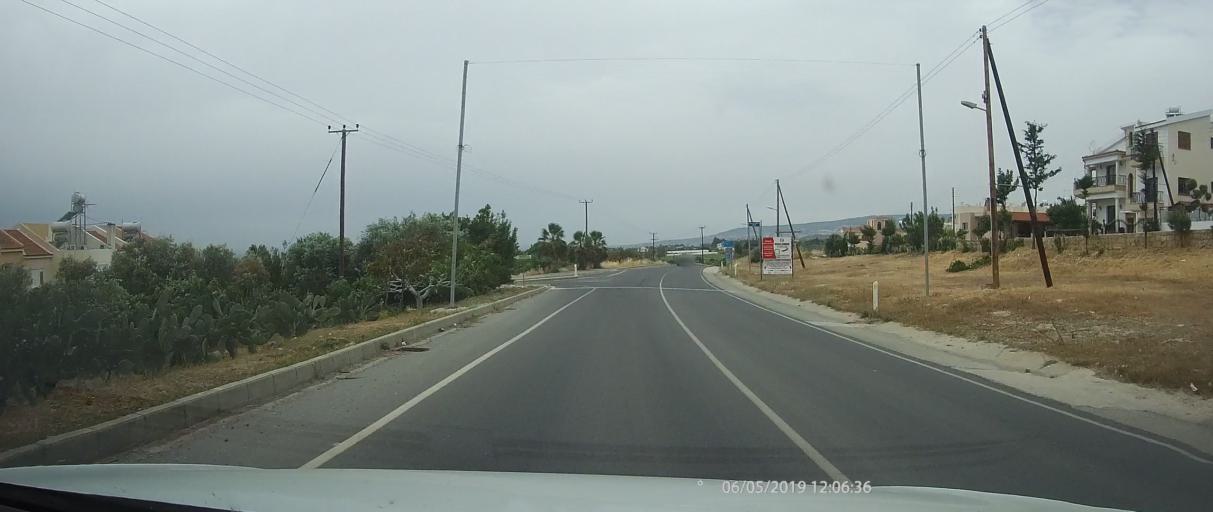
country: CY
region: Pafos
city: Empa
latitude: 34.8188
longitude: 32.4240
